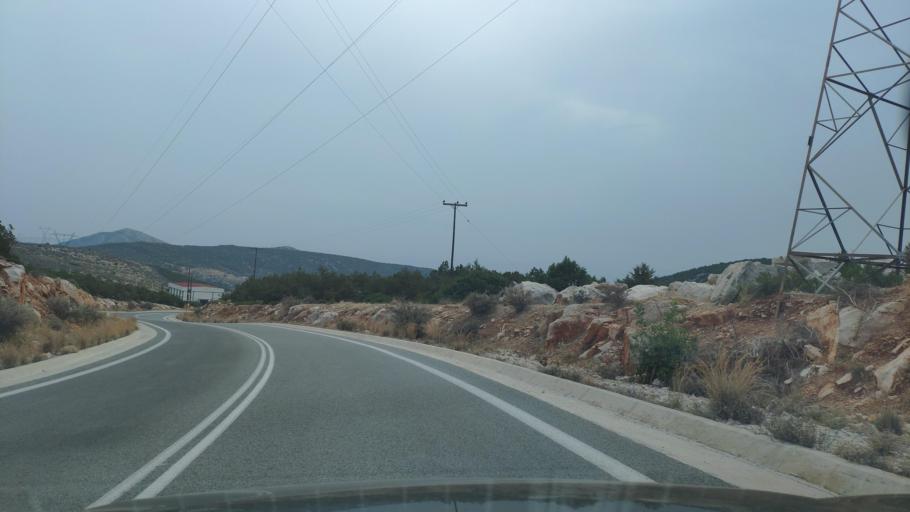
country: GR
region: Peloponnese
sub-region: Nomos Argolidos
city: Didyma
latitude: 37.4476
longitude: 23.1890
